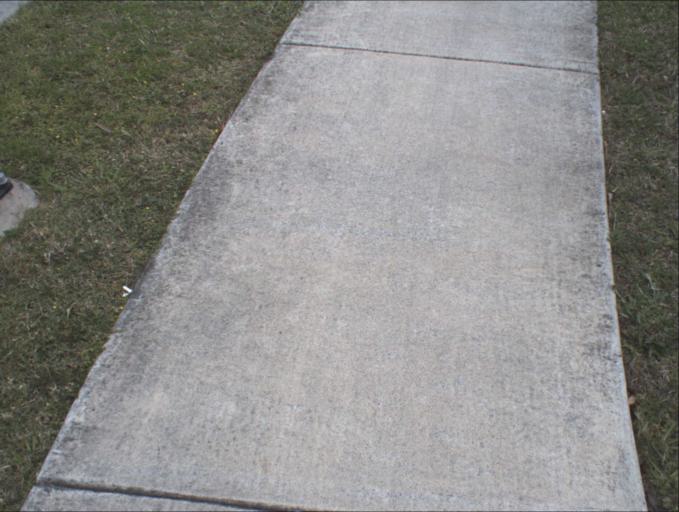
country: AU
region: Queensland
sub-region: Logan
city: Waterford West
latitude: -27.6846
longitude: 153.1360
